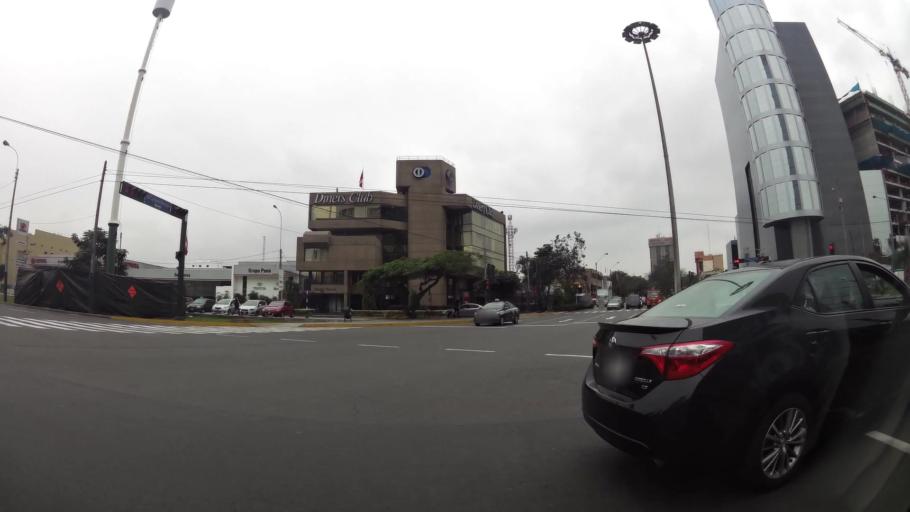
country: PE
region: Lima
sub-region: Lima
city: San Luis
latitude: -12.0974
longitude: -77.0206
